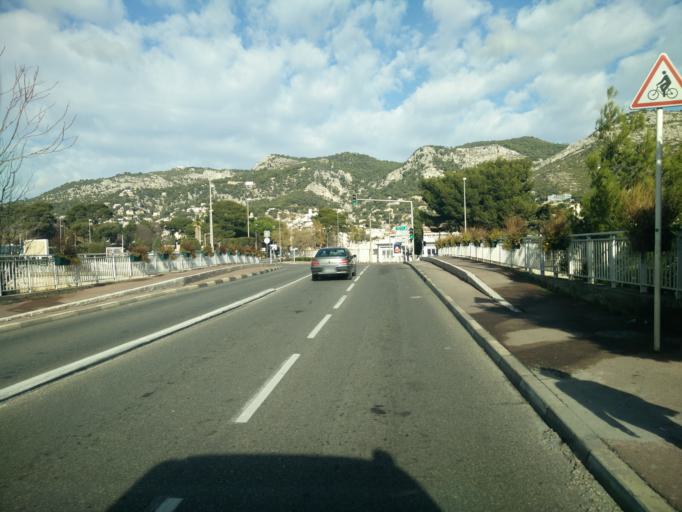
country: FR
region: Provence-Alpes-Cote d'Azur
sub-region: Departement du Var
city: Toulon
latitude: 43.1253
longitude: 5.9371
